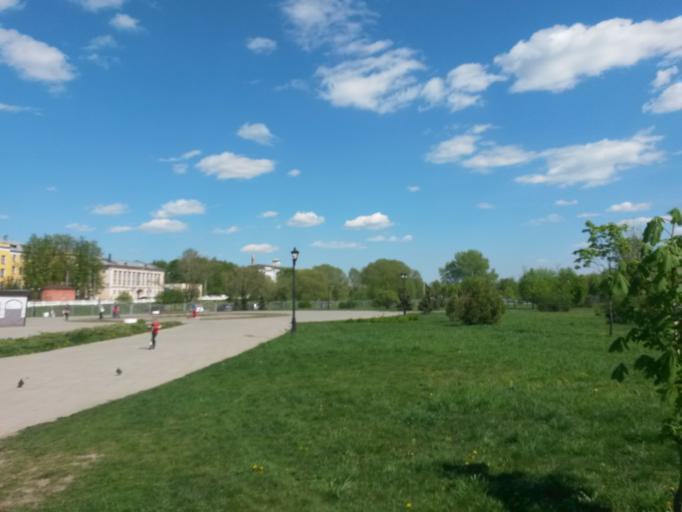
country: RU
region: Jaroslavl
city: Yaroslavl
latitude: 57.6183
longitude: 39.8708
